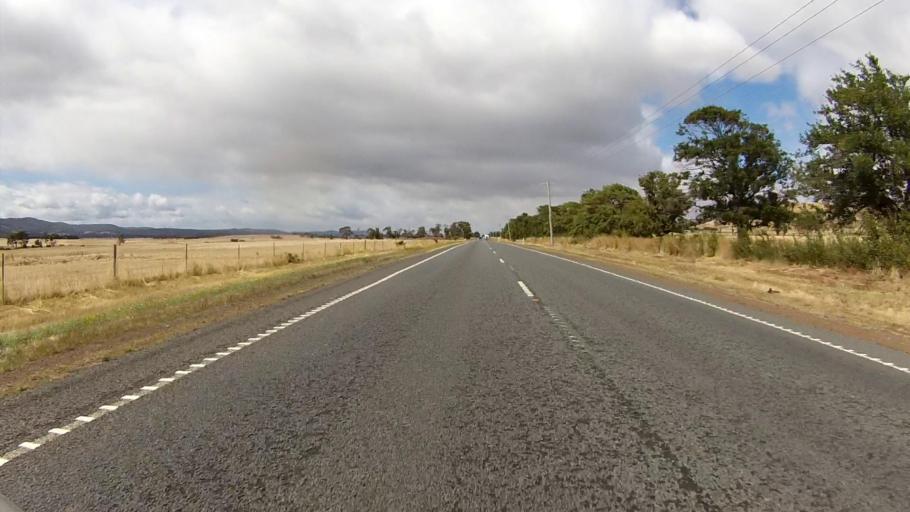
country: AU
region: Tasmania
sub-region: Northern Midlands
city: Evandale
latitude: -41.9706
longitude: 147.5018
